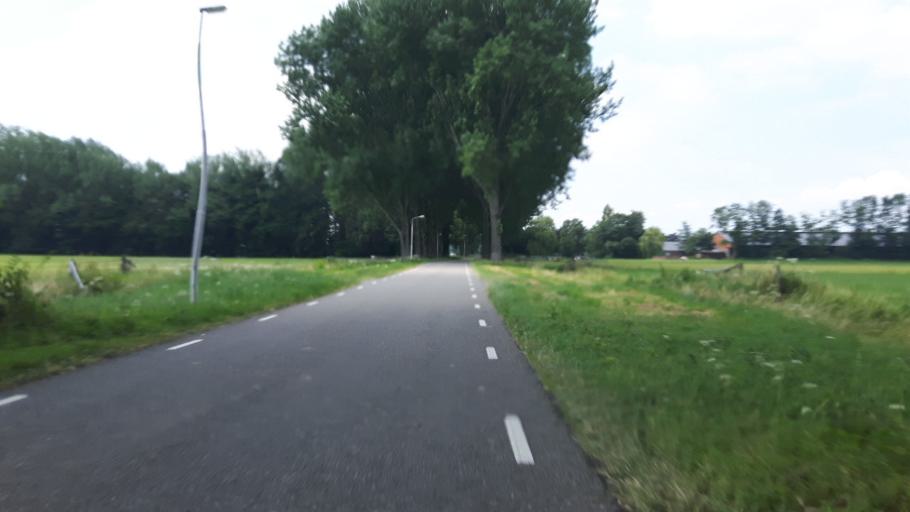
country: NL
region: Utrecht
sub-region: Gemeente Lopik
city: Lopik
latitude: 51.9188
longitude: 4.9695
